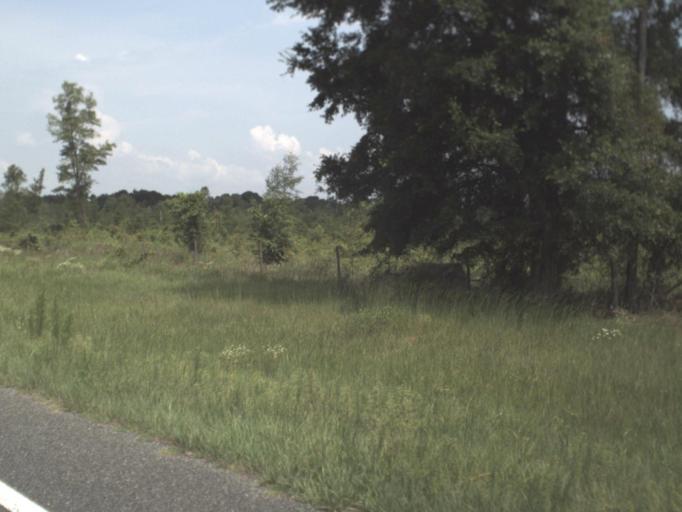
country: US
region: Florida
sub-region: Levy County
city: Chiefland
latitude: 29.4751
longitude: -82.7748
